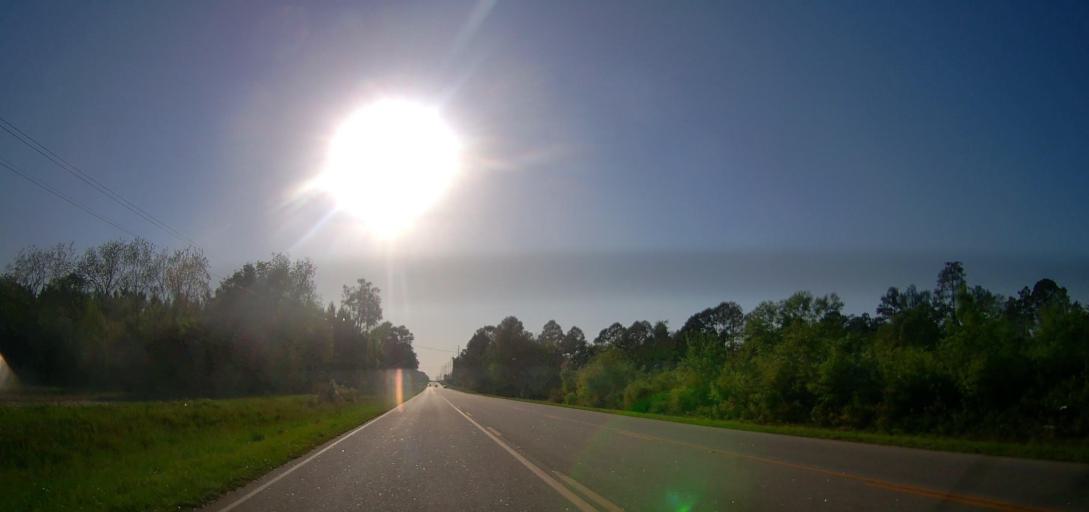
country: US
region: Georgia
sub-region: Ben Hill County
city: Fitzgerald
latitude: 31.7133
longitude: -83.2103
